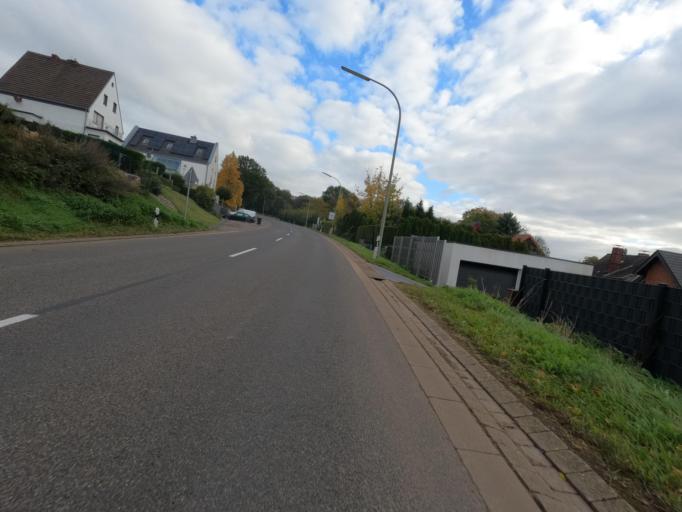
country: DE
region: North Rhine-Westphalia
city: Huckelhoven
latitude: 51.0498
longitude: 6.2519
